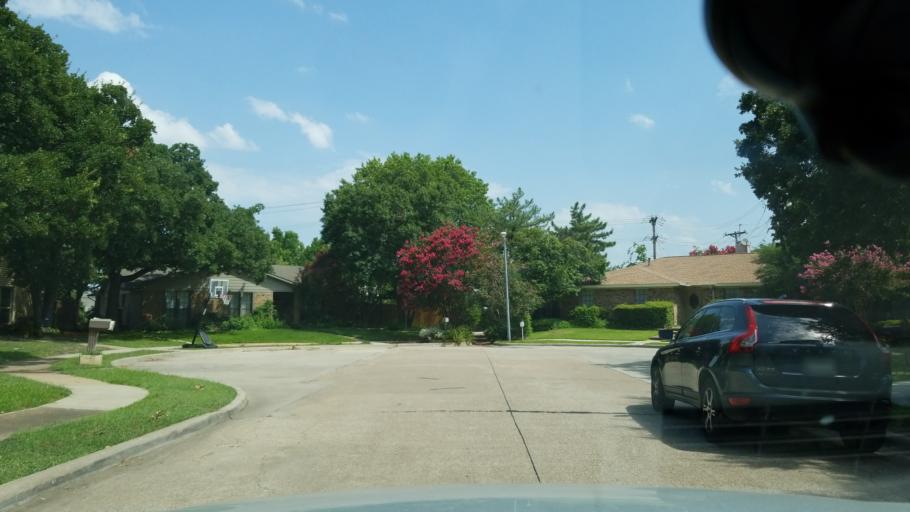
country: US
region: Texas
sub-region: Dallas County
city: Coppell
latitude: 32.9668
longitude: -96.9919
